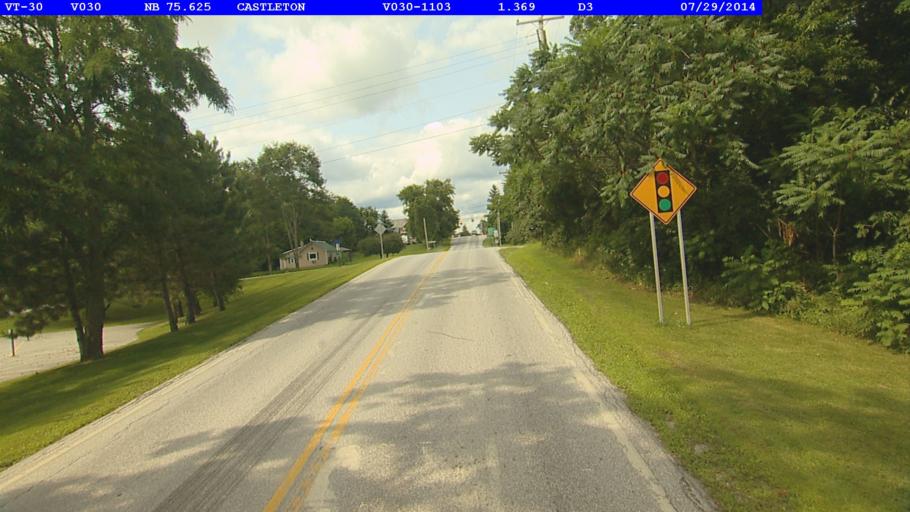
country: US
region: Vermont
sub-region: Rutland County
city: Castleton
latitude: 43.6064
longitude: -73.2089
